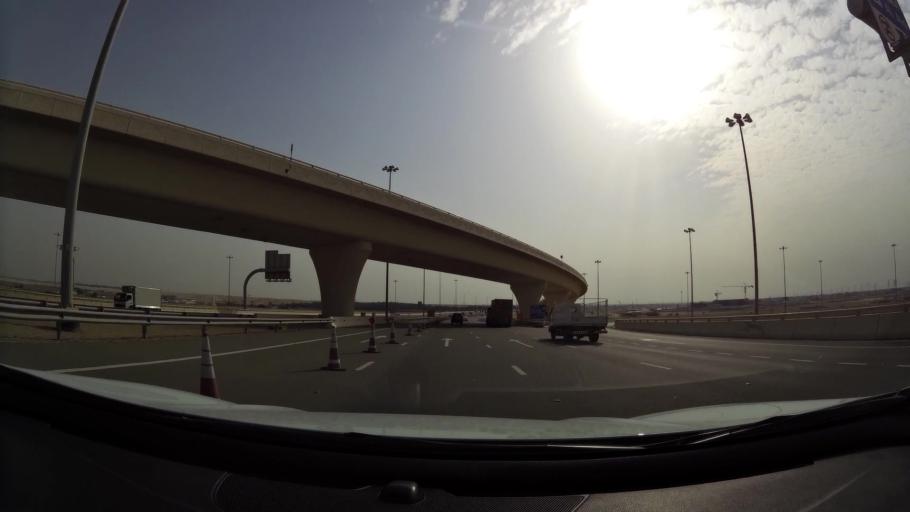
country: AE
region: Abu Dhabi
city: Abu Dhabi
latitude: 24.3079
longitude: 54.6003
